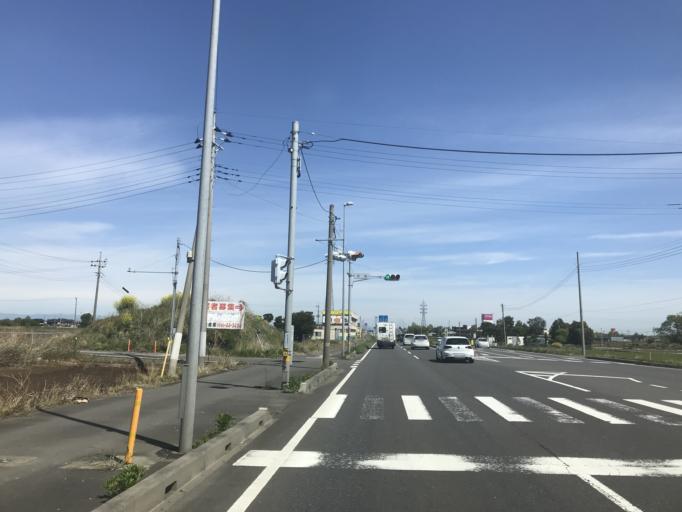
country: JP
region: Ibaraki
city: Ishige
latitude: 36.1825
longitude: 139.9896
